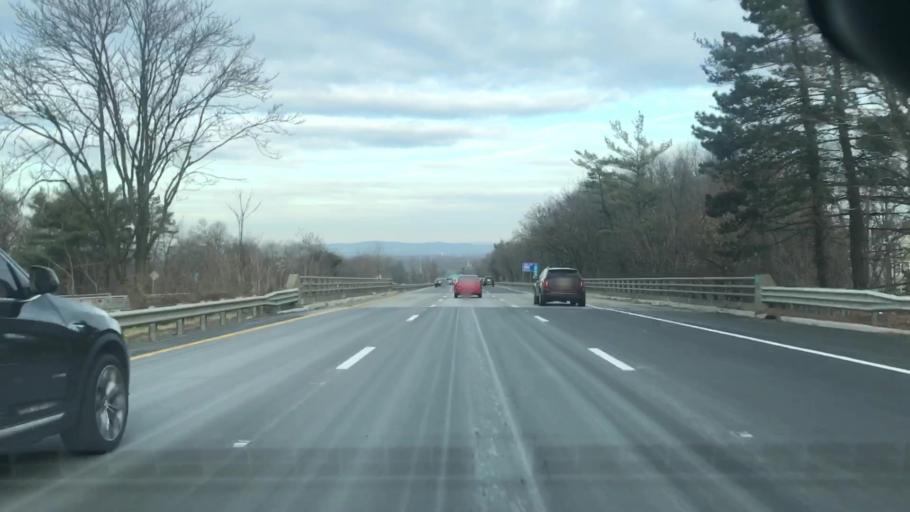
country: US
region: New Jersey
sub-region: Essex County
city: Roseland
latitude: 40.8183
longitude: -74.3149
